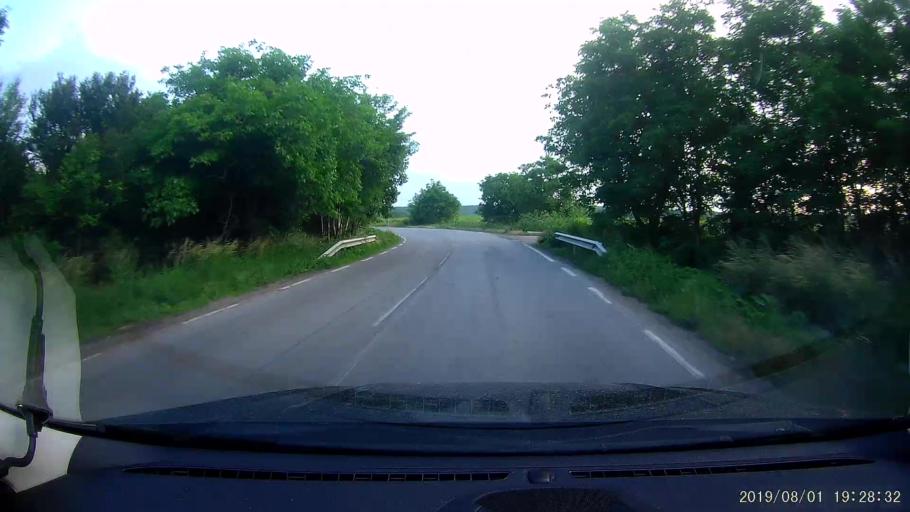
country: BG
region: Burgas
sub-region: Obshtina Sungurlare
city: Sungurlare
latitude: 42.8411
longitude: 26.9153
